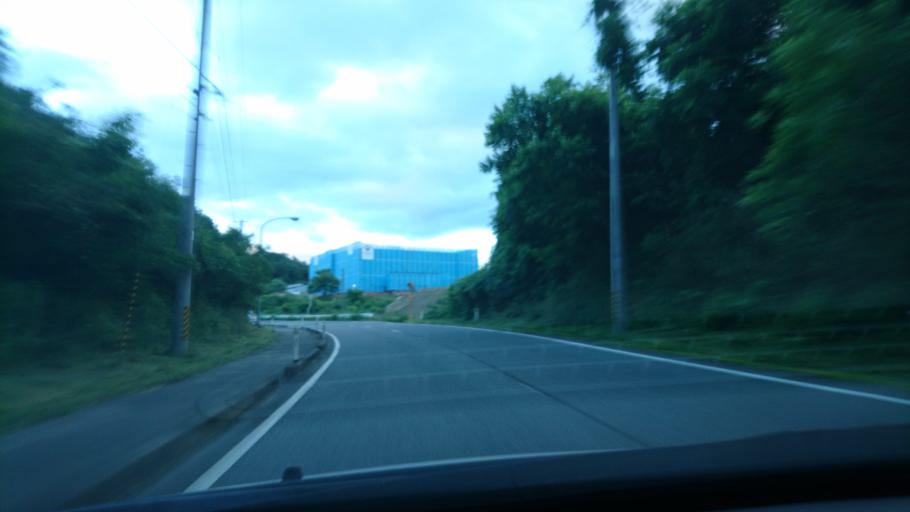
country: JP
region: Iwate
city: Ichinoseki
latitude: 38.7922
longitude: 141.0538
